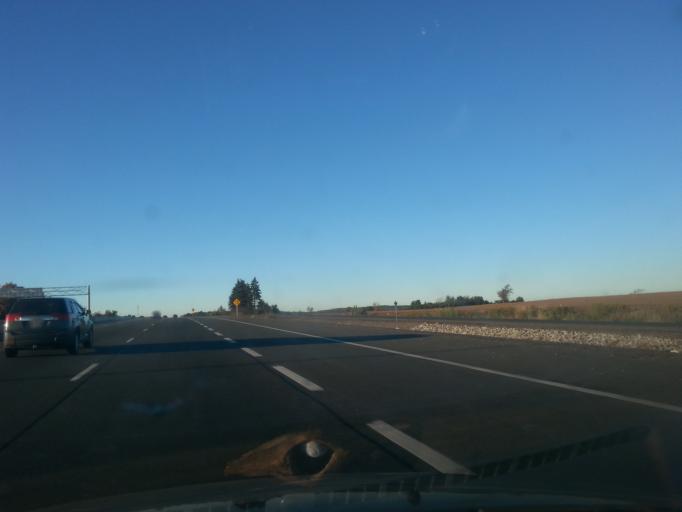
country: CA
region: Ontario
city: Vaughan
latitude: 43.9236
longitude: -79.5666
